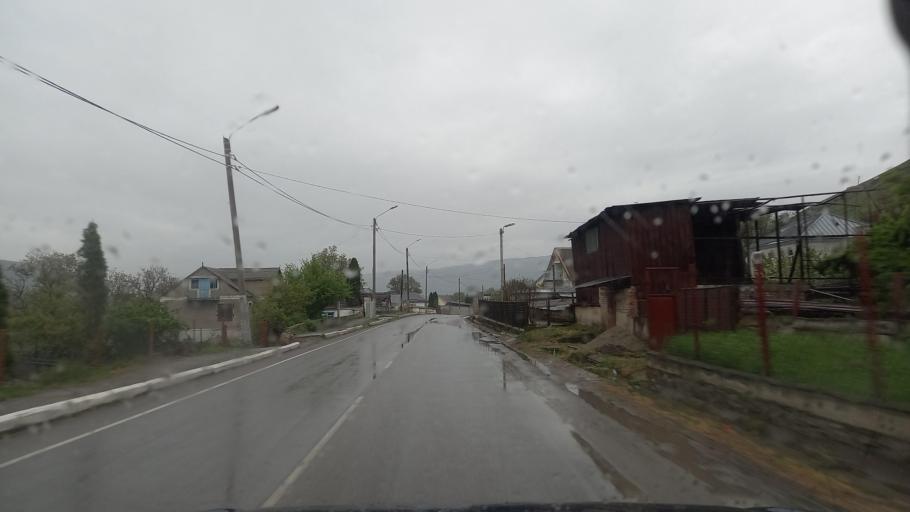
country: RU
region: Kabardino-Balkariya
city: Gundelen
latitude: 43.5923
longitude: 43.1853
